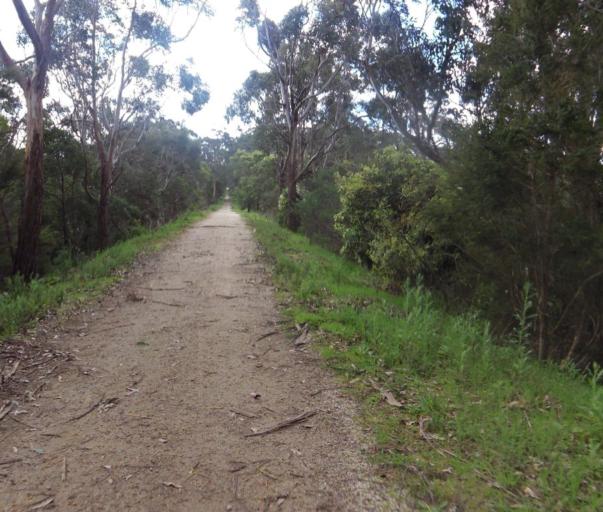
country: AU
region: Victoria
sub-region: Bass Coast
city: North Wonthaggi
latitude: -38.6618
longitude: 146.0249
